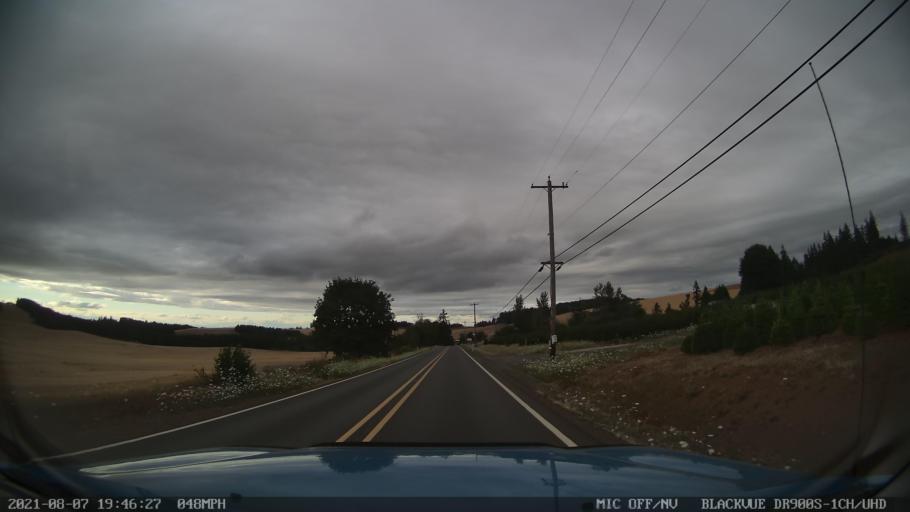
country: US
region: Oregon
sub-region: Marion County
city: Silverton
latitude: 44.9591
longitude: -122.7017
